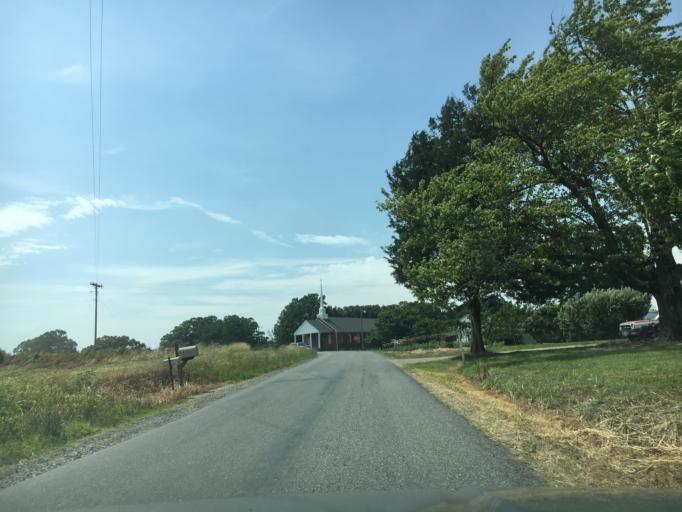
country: US
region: Virginia
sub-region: Pittsylvania County
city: Gretna
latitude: 36.9299
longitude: -79.4341
